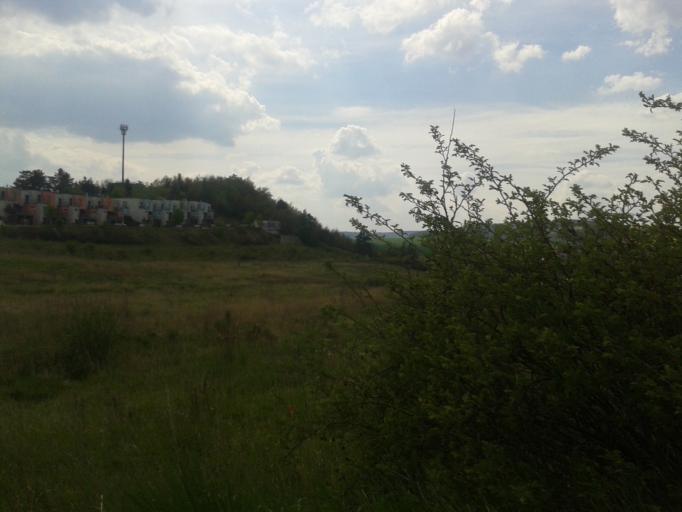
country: CZ
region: Central Bohemia
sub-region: Okres Beroun
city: Kraluv Dvur
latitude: 49.9535
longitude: 14.0352
